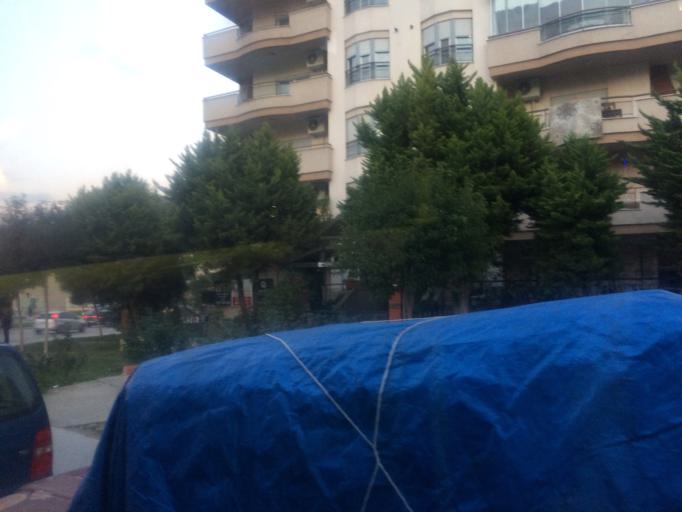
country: TR
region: Izmir
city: Karsiyaka
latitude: 38.4641
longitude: 27.0958
